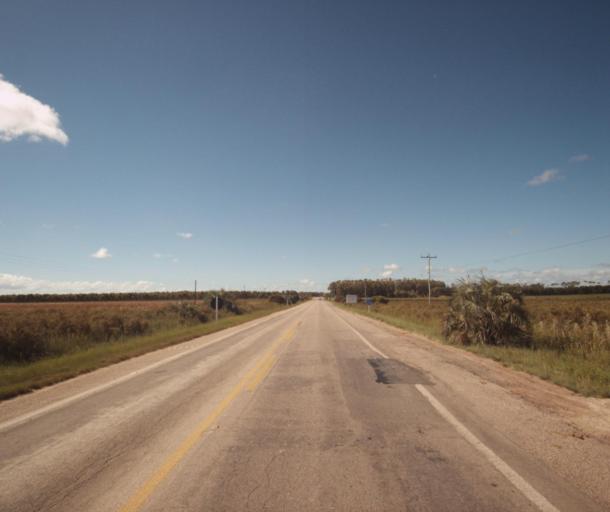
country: BR
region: Rio Grande do Sul
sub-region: Santa Vitoria Do Palmar
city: Santa Vitoria do Palmar
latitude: -33.5672
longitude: -53.3739
